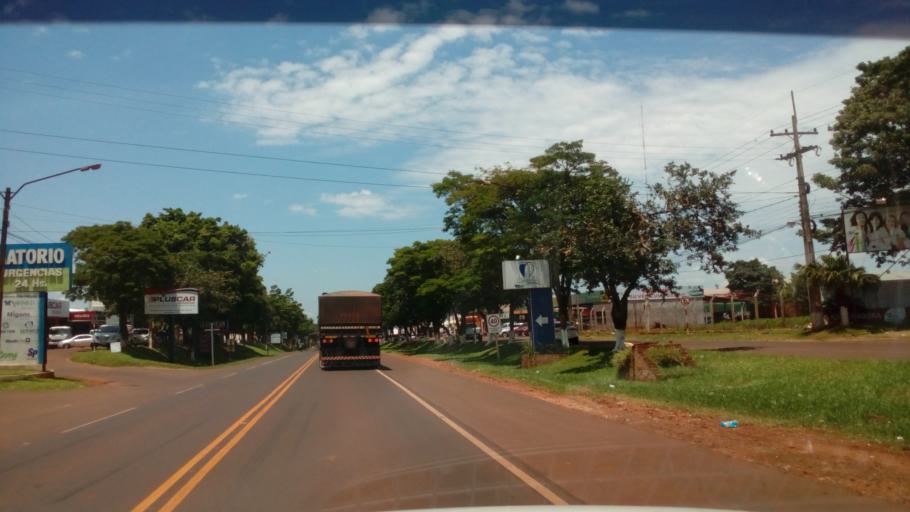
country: PY
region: Alto Parana
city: Santa Rita
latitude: -25.8008
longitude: -55.0927
